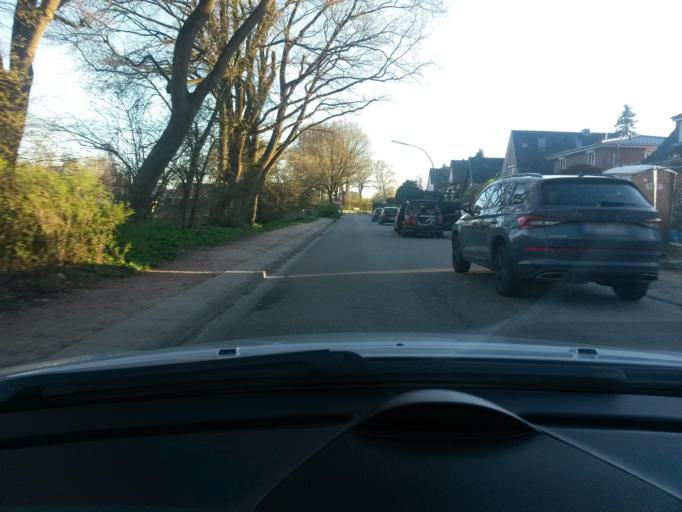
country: DE
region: Hamburg
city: Farmsen-Berne
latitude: 53.6127
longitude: 10.0959
